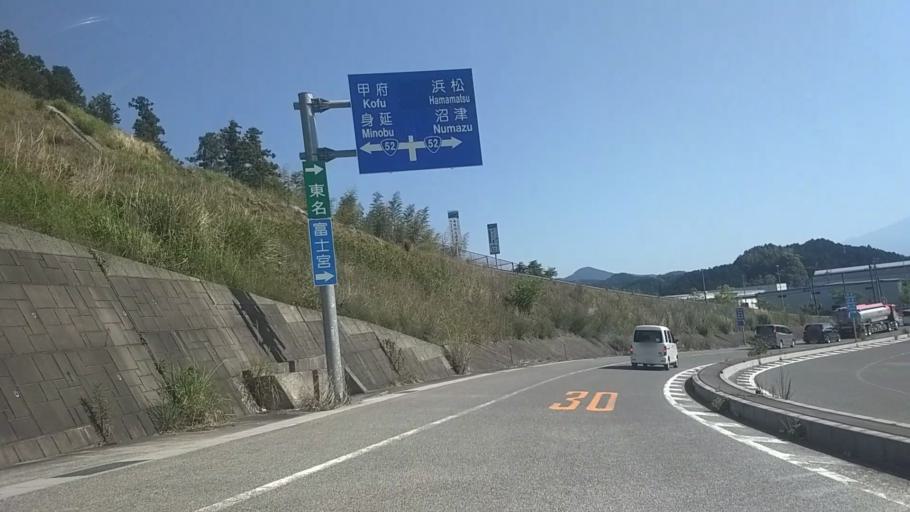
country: JP
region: Shizuoka
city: Fujinomiya
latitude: 35.1502
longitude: 138.5201
